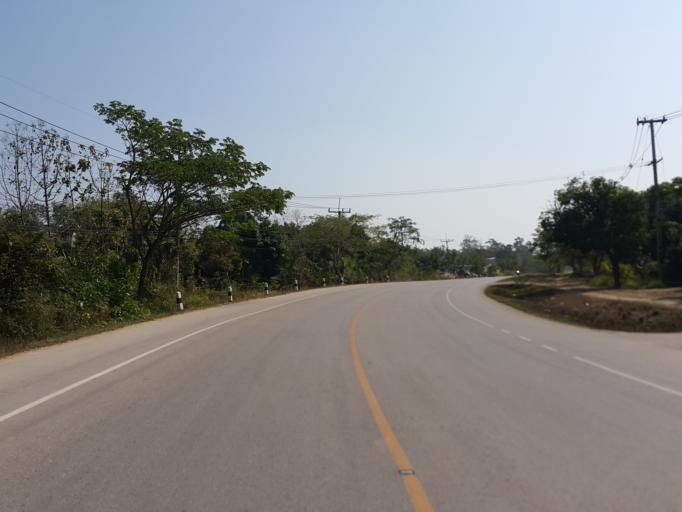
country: TH
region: Lampang
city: Chae Hom
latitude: 18.7439
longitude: 99.5772
